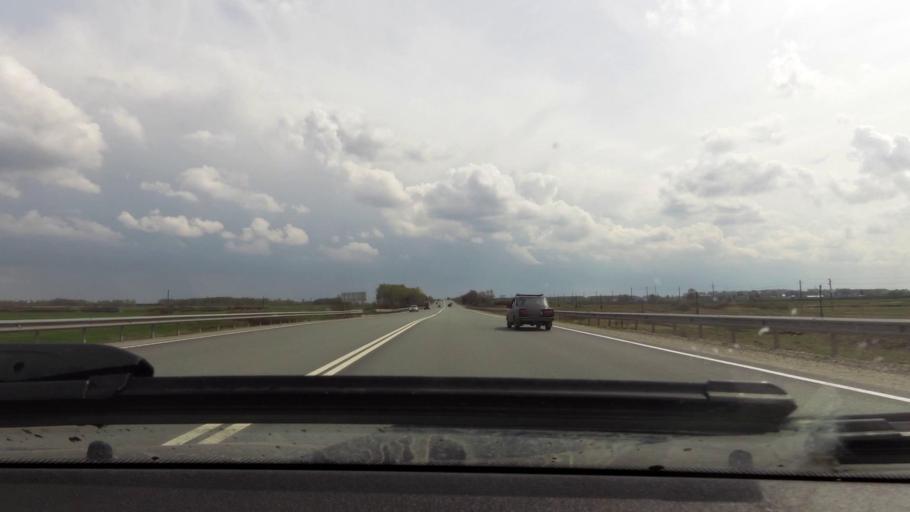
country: RU
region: Rjazan
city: Bagramovo
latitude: 54.7419
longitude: 39.4414
